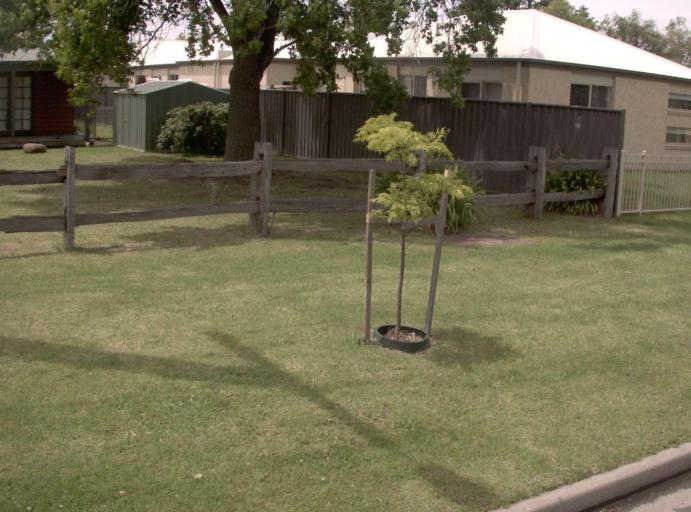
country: AU
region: Victoria
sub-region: Wellington
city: Sale
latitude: -38.0951
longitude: 147.0688
